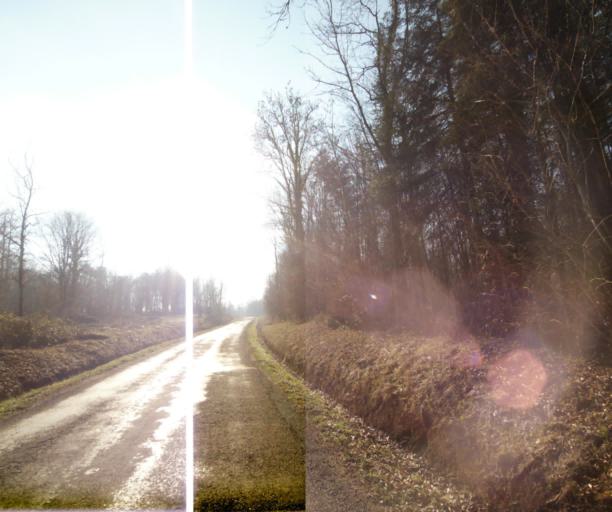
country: FR
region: Champagne-Ardenne
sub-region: Departement de la Haute-Marne
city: Wassy
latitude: 48.5166
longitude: 4.9701
